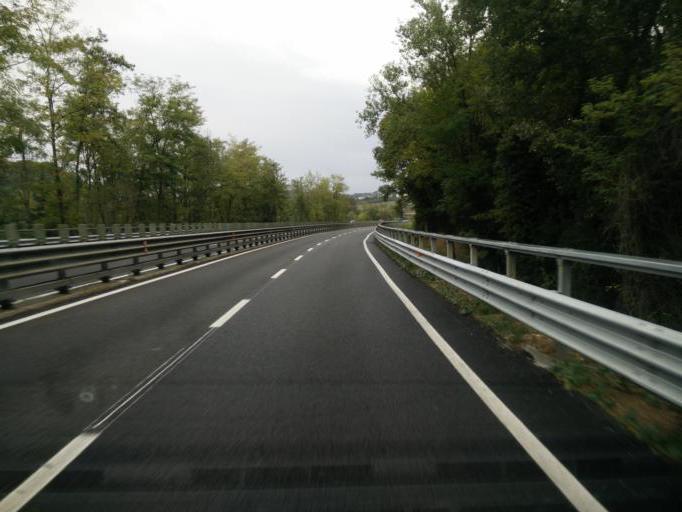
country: IT
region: Tuscany
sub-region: Provincia di Siena
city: Bellavista
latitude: 43.4531
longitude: 11.1555
